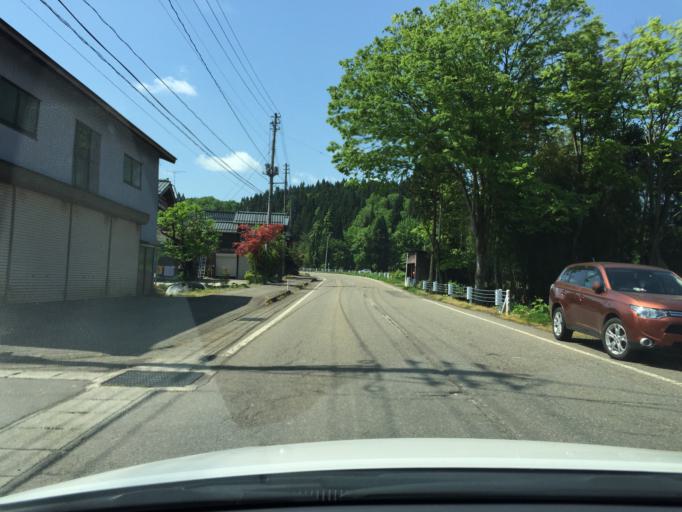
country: JP
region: Niigata
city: Tochio-honcho
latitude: 37.5407
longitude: 139.0926
